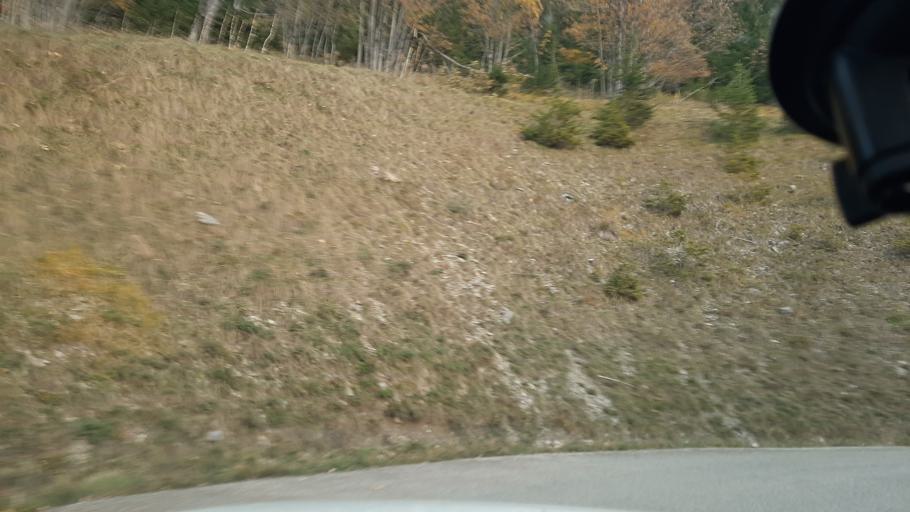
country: FR
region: Rhone-Alpes
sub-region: Departement de la Savoie
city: Villargondran
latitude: 45.1968
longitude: 6.3110
